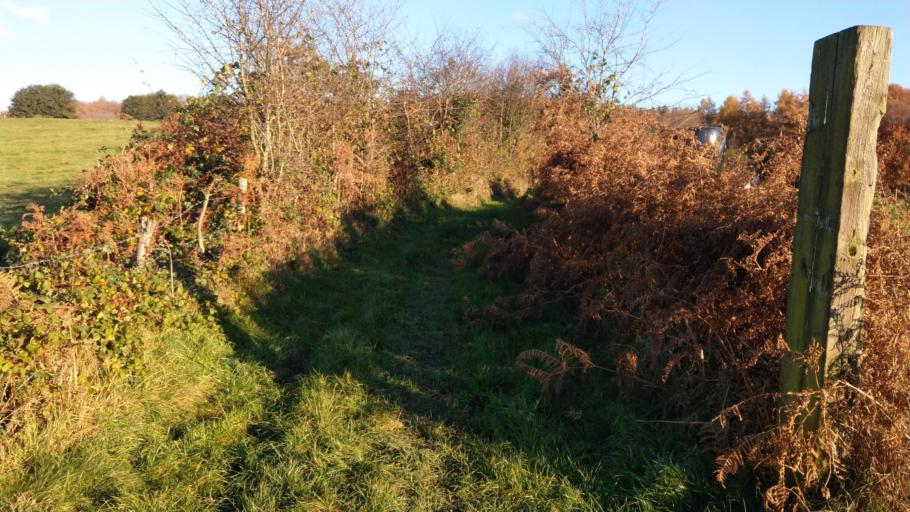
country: BE
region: Wallonia
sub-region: Province de Liege
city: La Calamine
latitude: 50.7385
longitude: 6.0028
